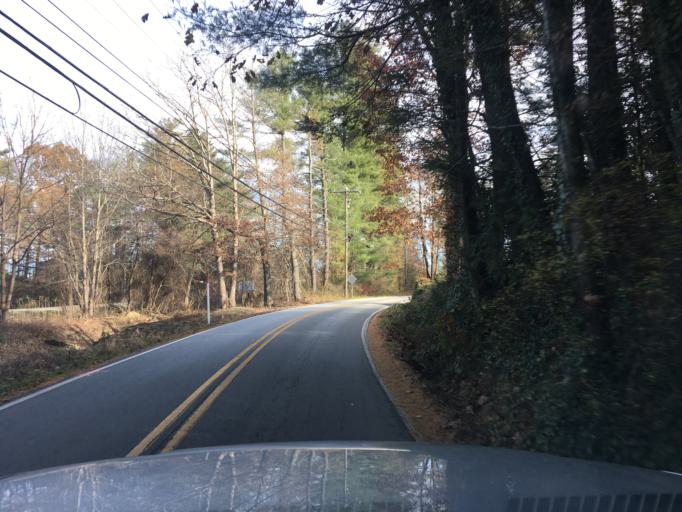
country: US
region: North Carolina
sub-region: Henderson County
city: Laurel Park
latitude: 35.3213
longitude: -82.4961
